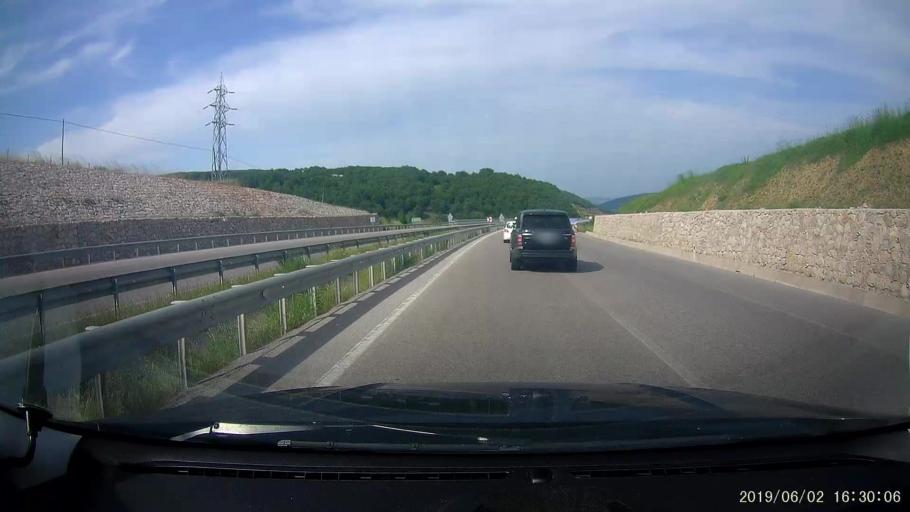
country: TR
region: Samsun
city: Ladik
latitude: 41.0225
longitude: 35.8757
